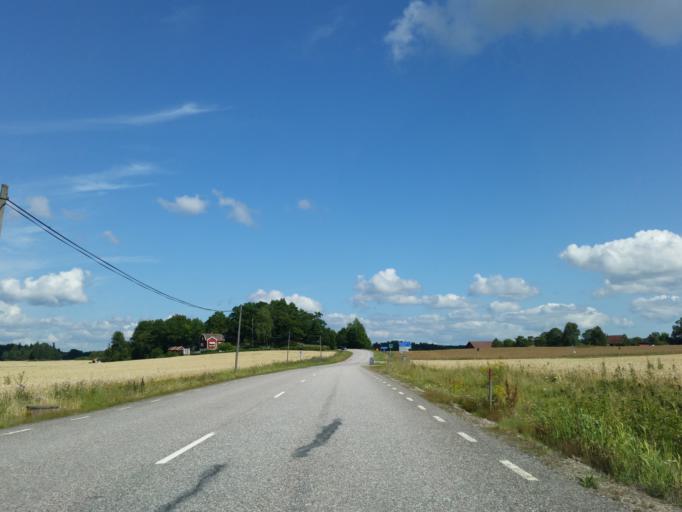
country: SE
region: Soedermanland
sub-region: Trosa Kommun
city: Vagnharad
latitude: 58.9905
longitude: 17.6425
